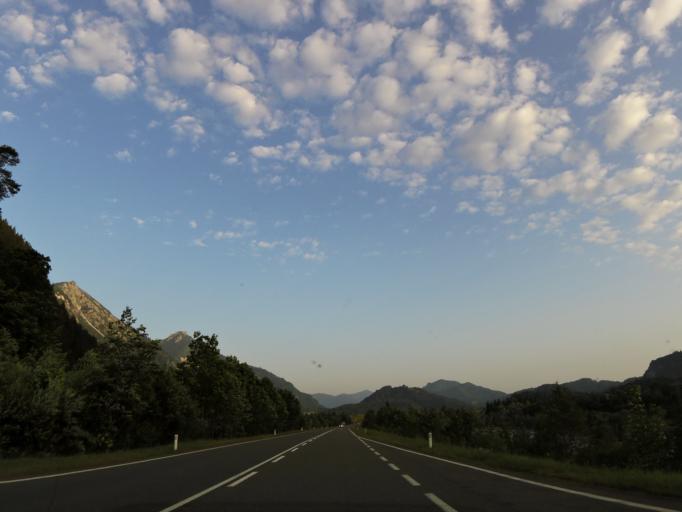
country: AT
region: Tyrol
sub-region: Politischer Bezirk Reutte
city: Pflach
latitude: 47.5263
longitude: 10.6976
